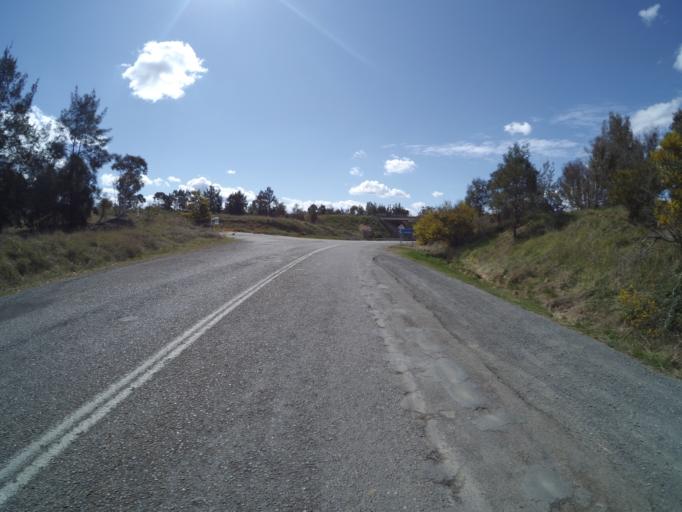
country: AU
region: New South Wales
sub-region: Goulburn Mulwaree
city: Goulburn
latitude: -34.7769
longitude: 149.7064
